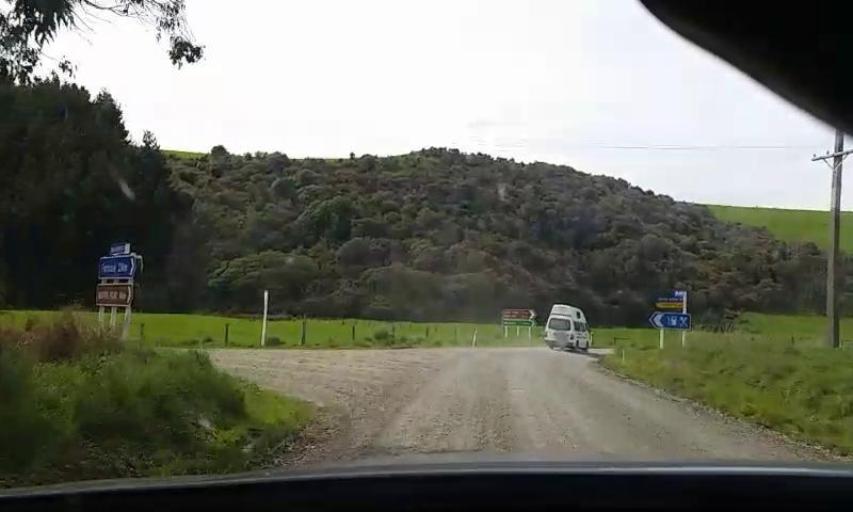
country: NZ
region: Otago
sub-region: Clutha District
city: Papatowai
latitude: -46.6252
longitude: 168.9974
